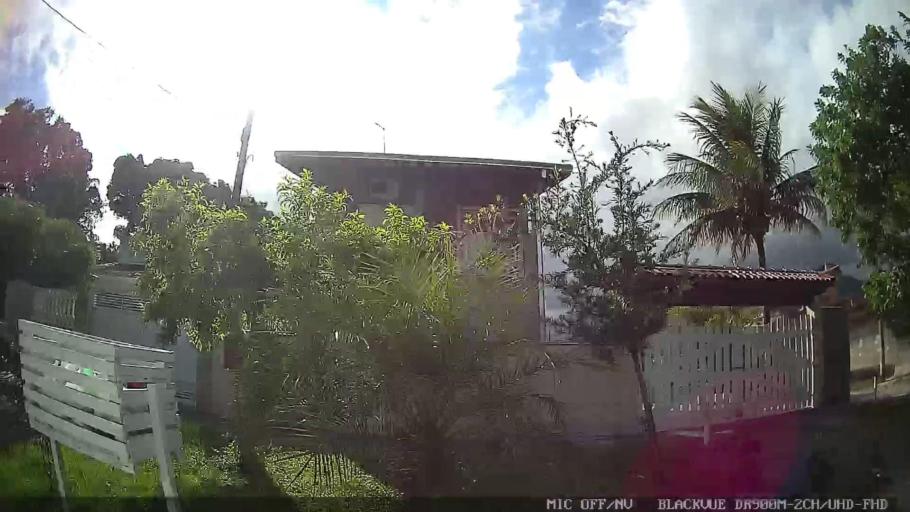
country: BR
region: Sao Paulo
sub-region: Caraguatatuba
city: Caraguatatuba
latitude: -23.6422
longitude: -45.4437
